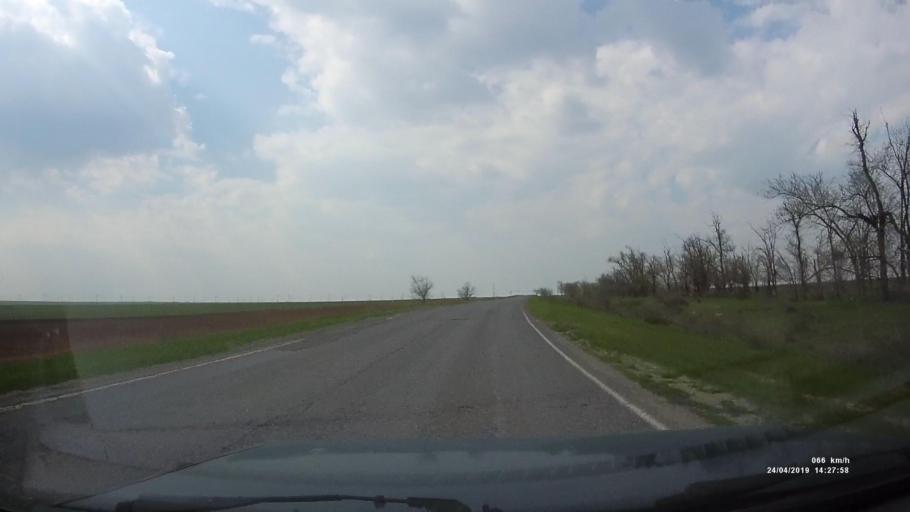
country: RU
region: Kalmykiya
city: Arshan'
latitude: 46.3350
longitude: 44.0341
